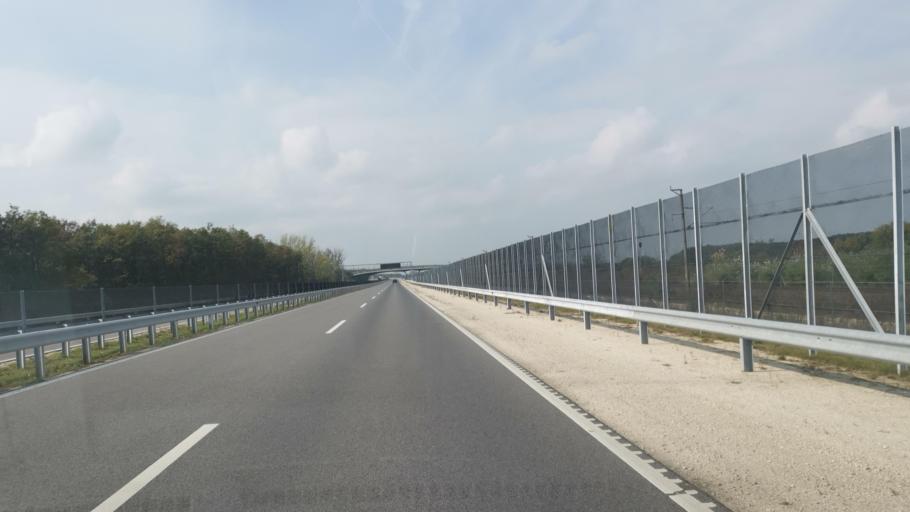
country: HU
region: Gyor-Moson-Sopron
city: Kapuvar
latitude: 47.5850
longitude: 16.9636
